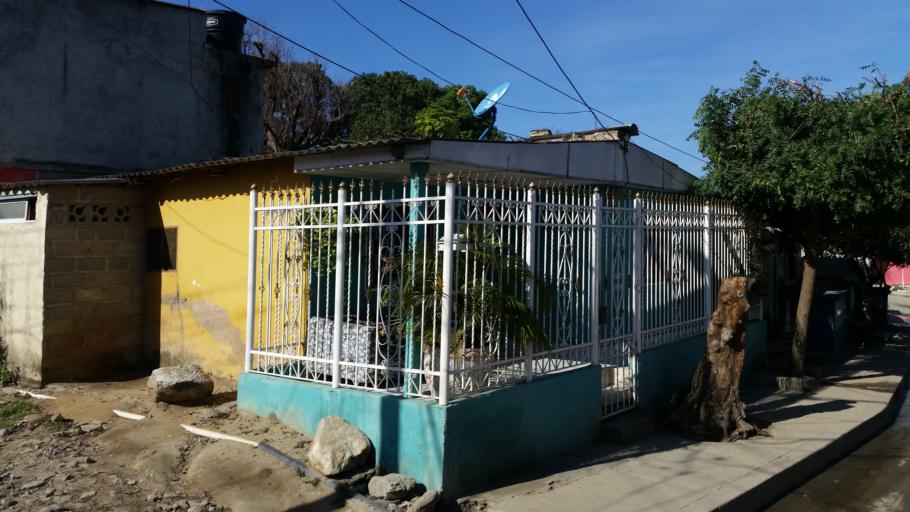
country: CO
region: Magdalena
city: Santa Marta
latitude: 11.1492
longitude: -74.2180
